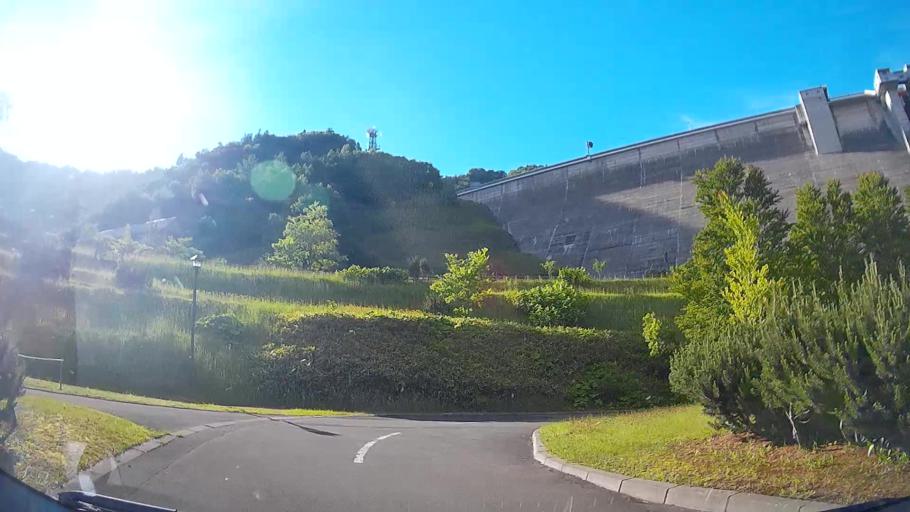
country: JP
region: Hokkaido
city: Sapporo
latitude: 42.9831
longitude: 141.1567
